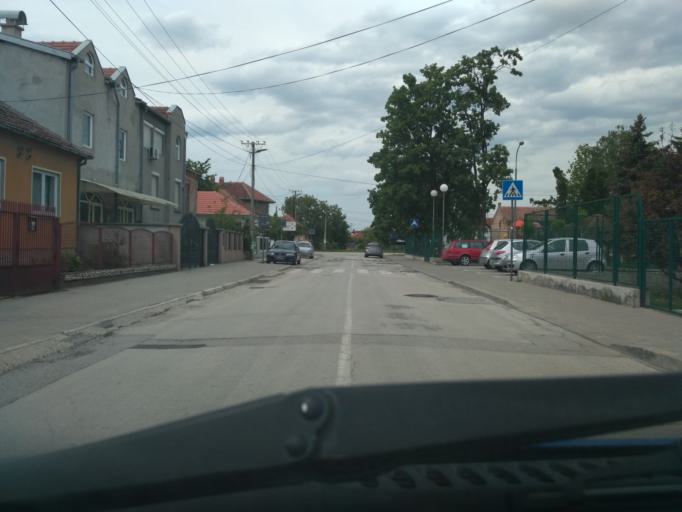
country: RS
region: Central Serbia
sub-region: Pomoravski Okrug
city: Svilajnac
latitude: 44.2327
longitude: 21.2019
